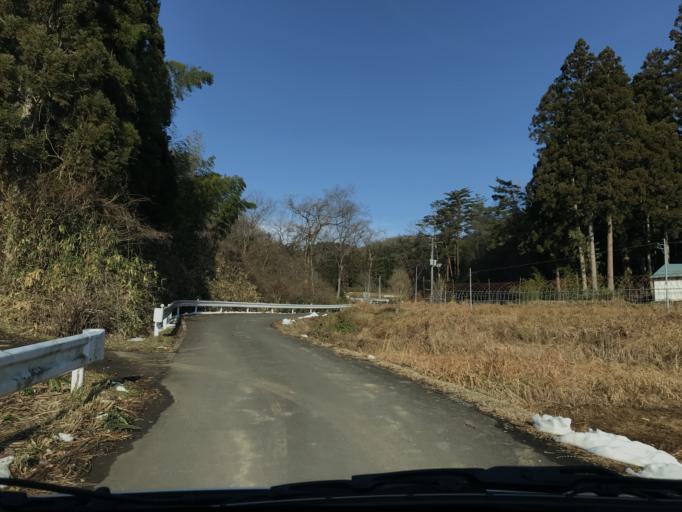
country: JP
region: Iwate
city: Ichinoseki
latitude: 38.9711
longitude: 141.0395
